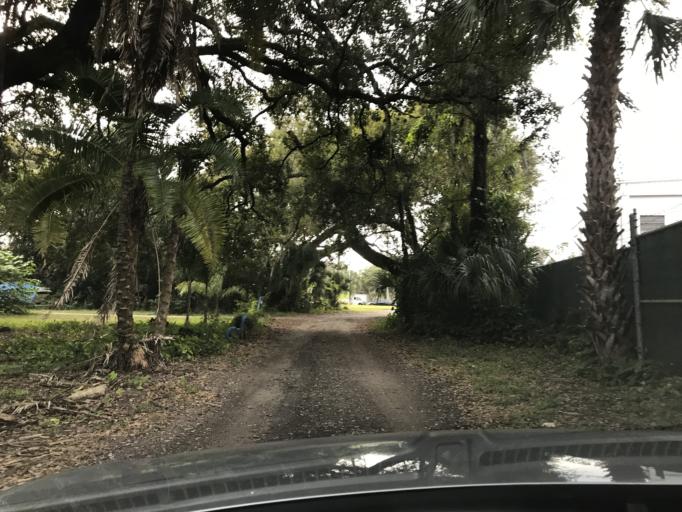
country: US
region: Florida
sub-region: Hillsborough County
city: Egypt Lake-Leto
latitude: 27.9969
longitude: -82.4681
